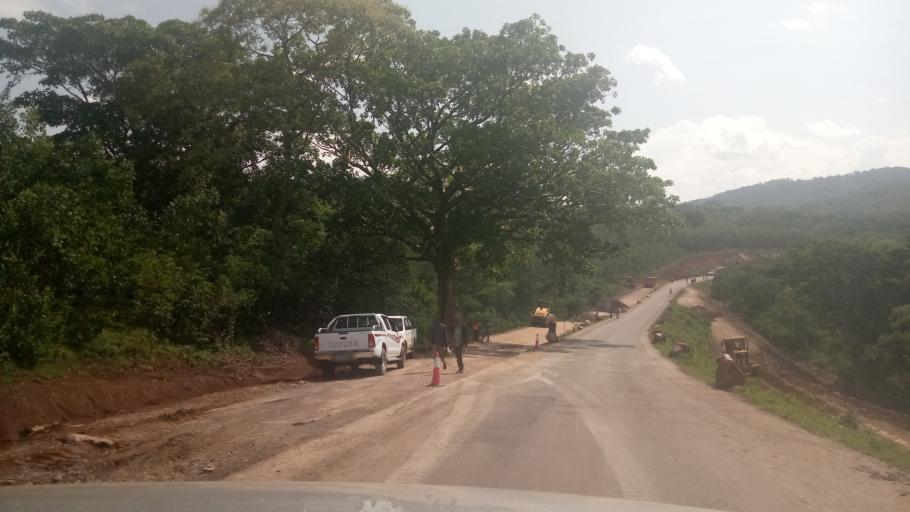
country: ET
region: Oromiya
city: Agaro
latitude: 7.9916
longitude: 36.5083
